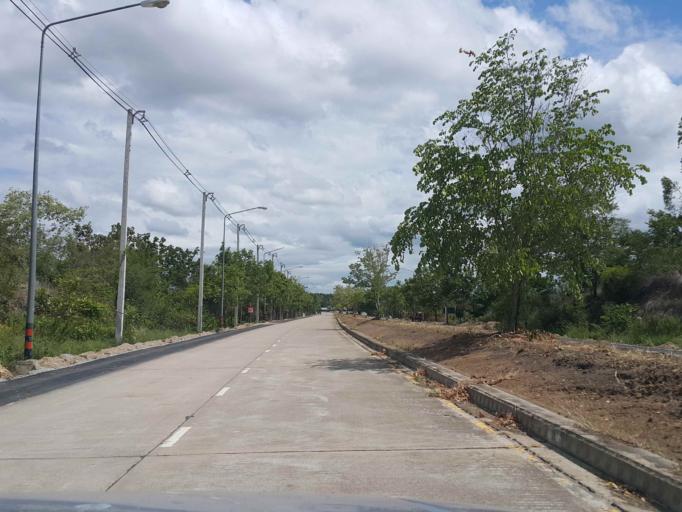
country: TH
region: Tak
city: Tak
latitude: 16.8594
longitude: 99.1153
